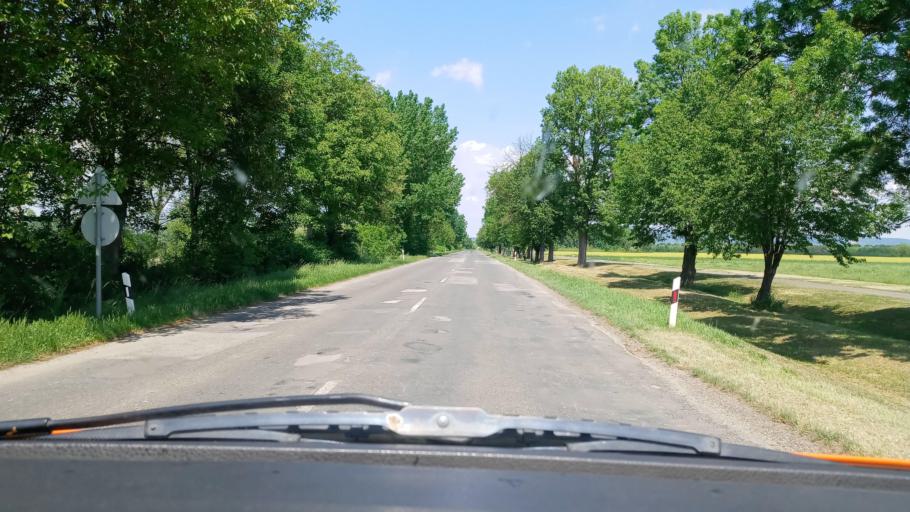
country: HU
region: Baranya
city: Harkany
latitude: 45.8124
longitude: 18.2144
